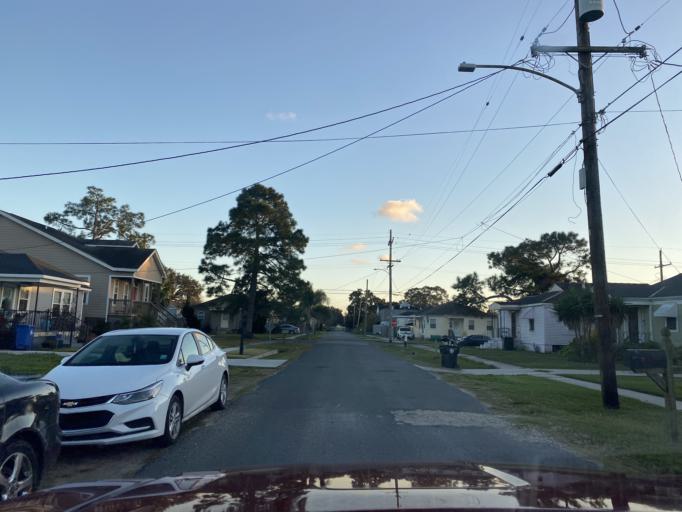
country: US
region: Louisiana
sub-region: Orleans Parish
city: New Orleans
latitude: 30.0199
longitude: -90.0528
